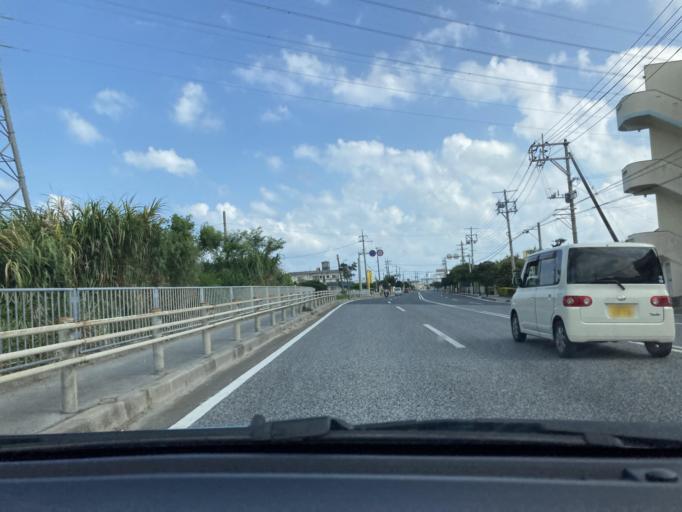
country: JP
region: Okinawa
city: Chatan
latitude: 26.2905
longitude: 127.8121
